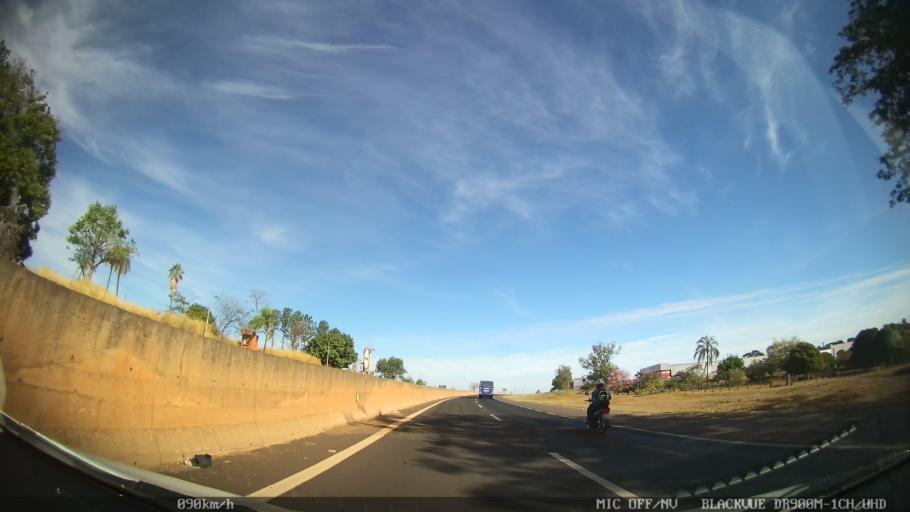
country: BR
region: Sao Paulo
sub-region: Sao Jose Do Rio Preto
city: Sao Jose do Rio Preto
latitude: -20.7423
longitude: -49.3380
